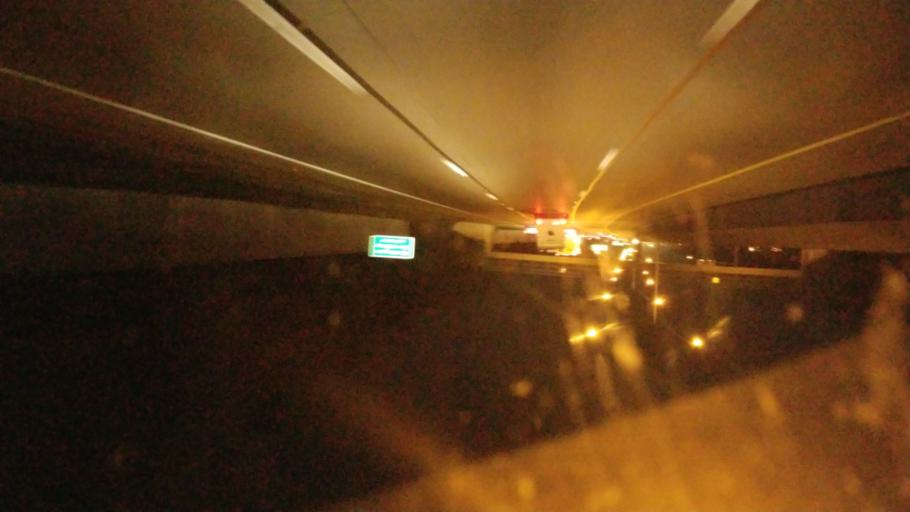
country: US
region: Ohio
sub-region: Franklin County
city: Worthington
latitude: 40.0741
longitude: -82.9881
